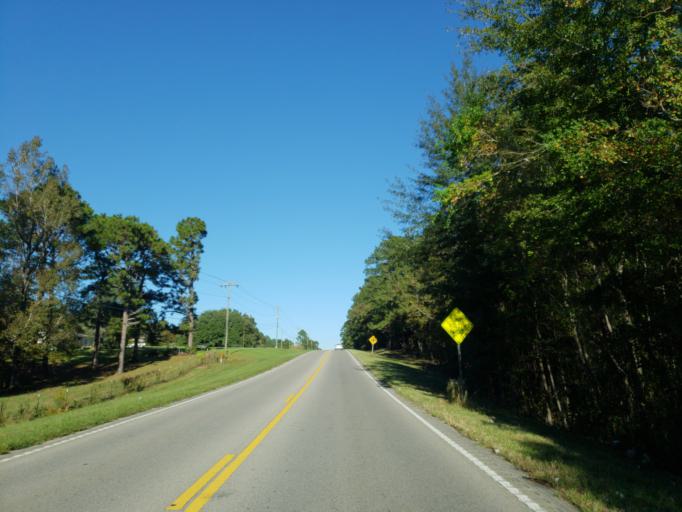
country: US
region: Mississippi
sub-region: Forrest County
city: Petal
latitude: 31.3577
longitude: -89.1593
